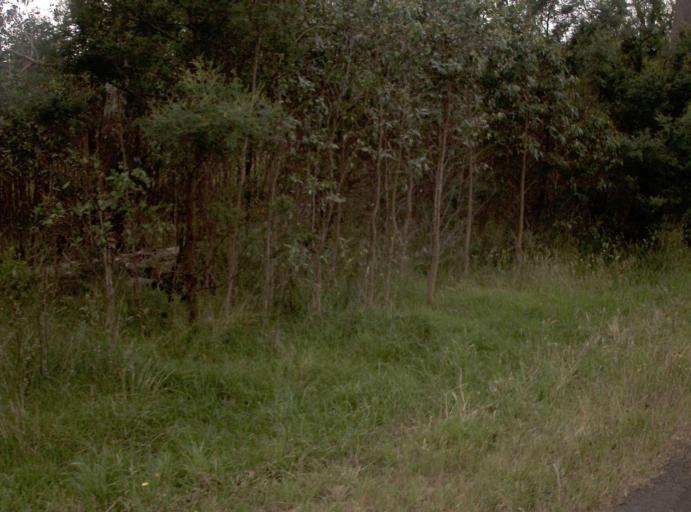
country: AU
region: Victoria
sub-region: Latrobe
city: Traralgon
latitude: -38.5584
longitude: 146.8085
